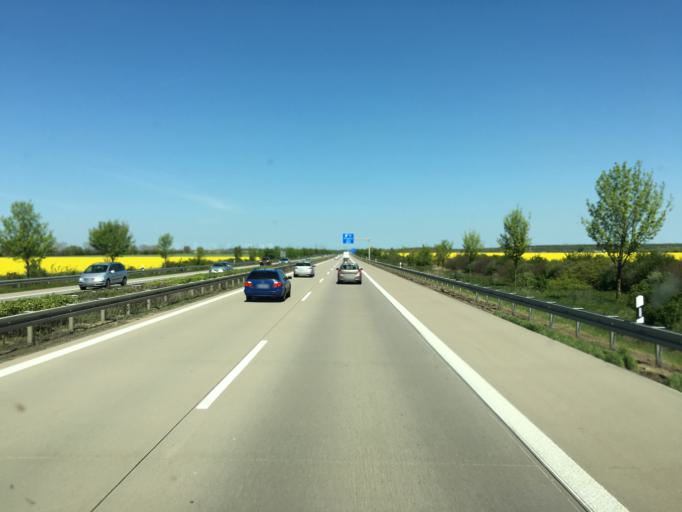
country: DE
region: Saxony-Anhalt
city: Geusa
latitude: 51.3563
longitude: 11.9169
